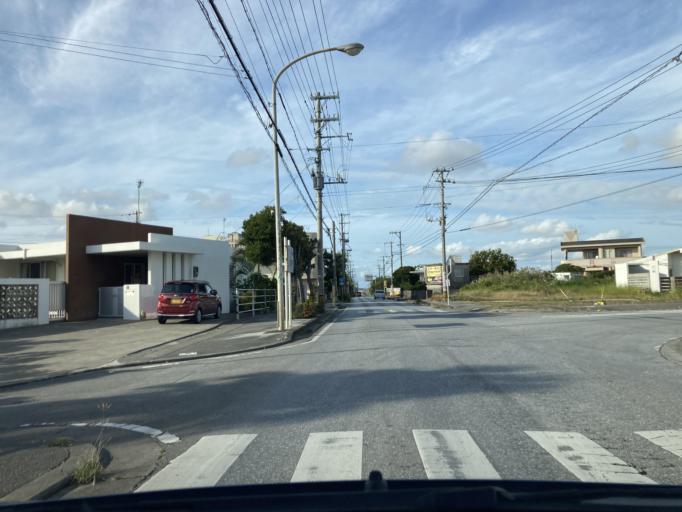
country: JP
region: Okinawa
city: Itoman
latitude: 26.1344
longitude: 127.7310
